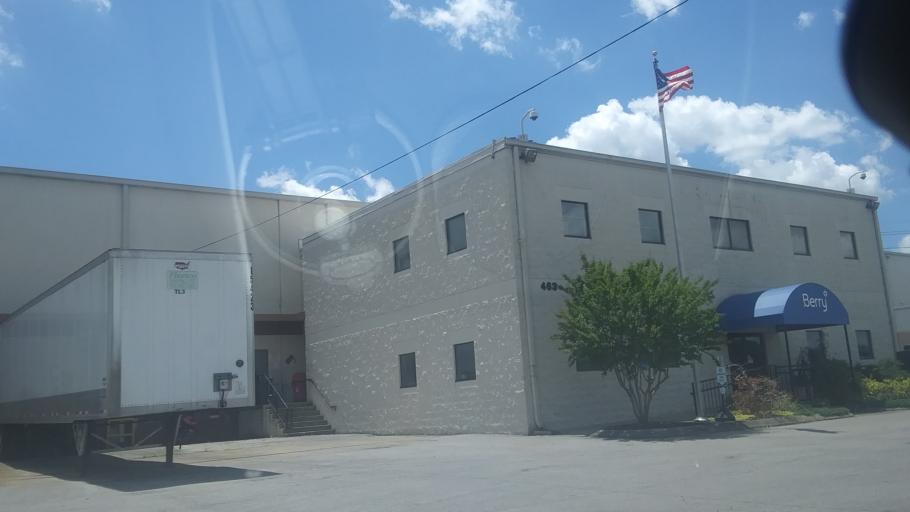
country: US
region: Tennessee
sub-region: Davidson County
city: Oak Hill
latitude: 36.0917
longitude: -86.6919
